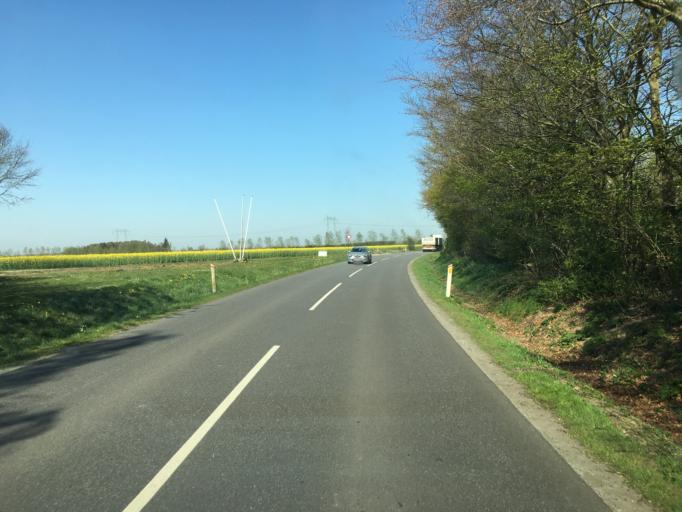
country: DK
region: South Denmark
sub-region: Aabenraa Kommune
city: Tinglev
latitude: 54.9948
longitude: 9.2941
